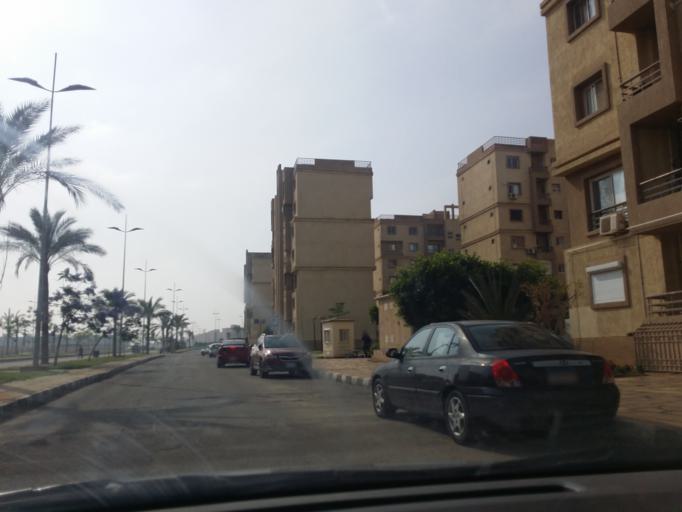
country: EG
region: Muhafazat al Qalyubiyah
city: Al Khankah
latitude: 30.0832
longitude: 31.6469
